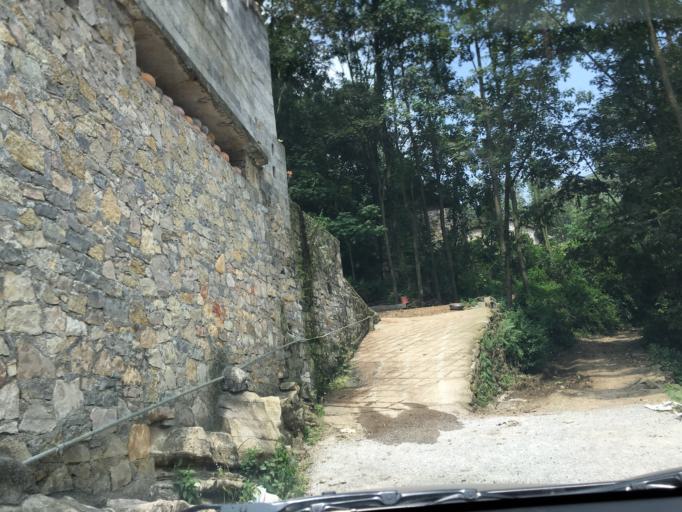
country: CN
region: Guizhou Sheng
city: Anshun
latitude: 25.5971
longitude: 105.6729
